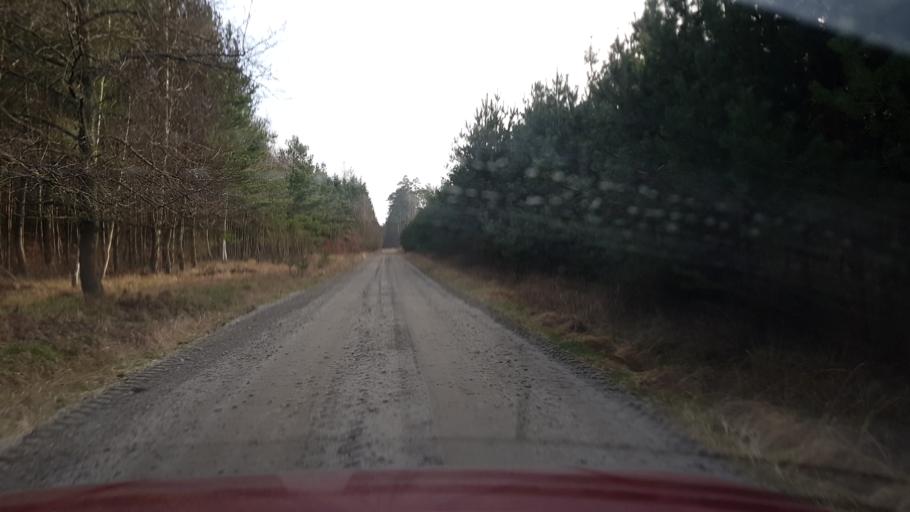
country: PL
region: West Pomeranian Voivodeship
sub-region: Powiat choszczenski
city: Pelczyce
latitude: 52.9265
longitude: 15.3667
